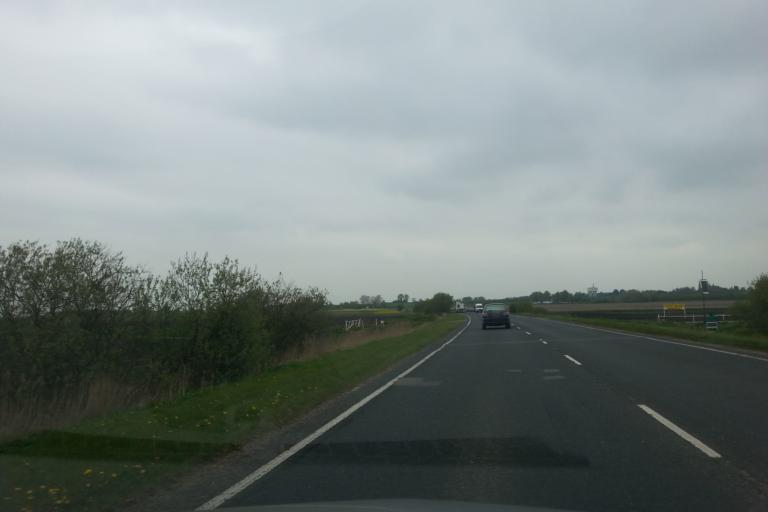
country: GB
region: England
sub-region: Cambridgeshire
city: Littleport
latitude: 52.4360
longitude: 0.2819
